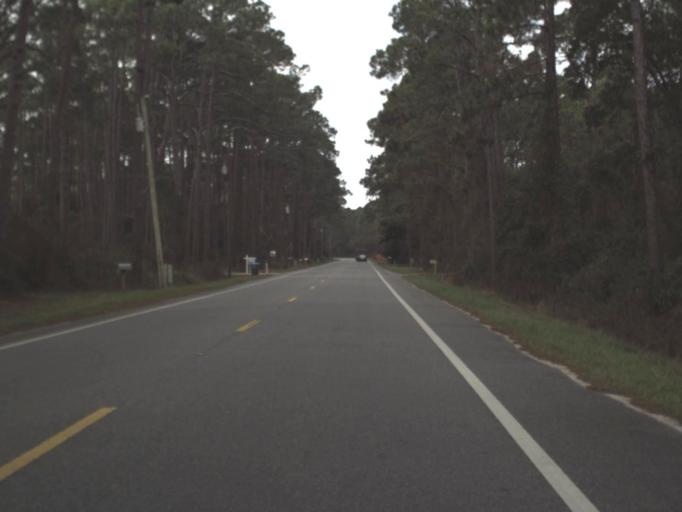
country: US
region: Florida
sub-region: Franklin County
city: Carrabelle
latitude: 29.8084
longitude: -84.7290
